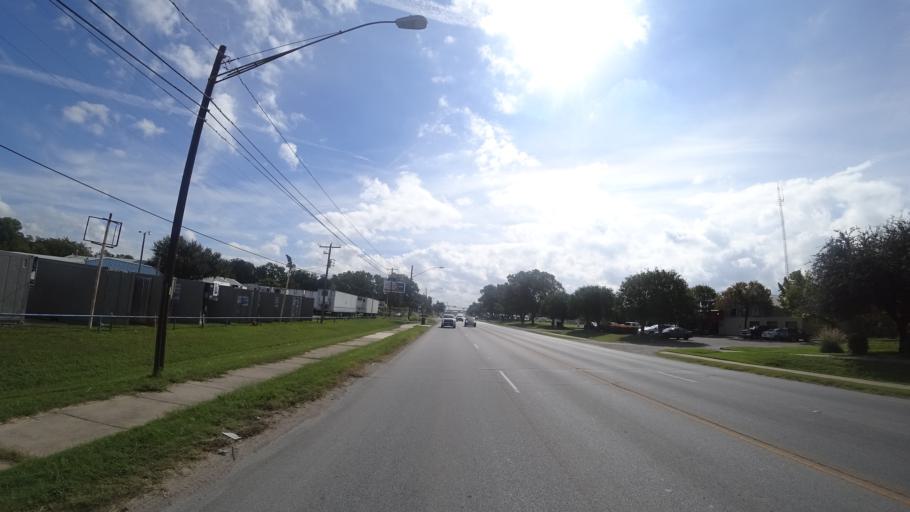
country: US
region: Texas
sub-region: Travis County
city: Austin
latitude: 30.2543
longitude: -97.6990
